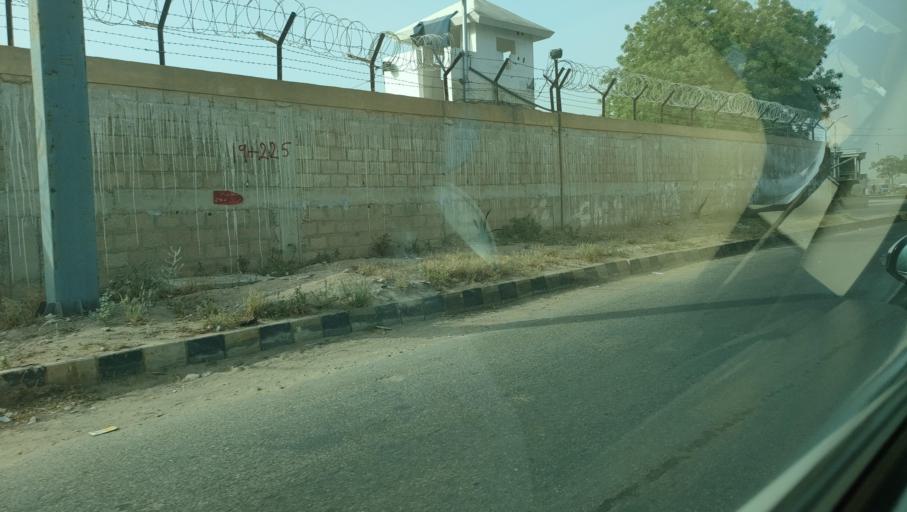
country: PK
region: Sindh
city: Malir Cantonment
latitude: 24.9129
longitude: 67.1865
